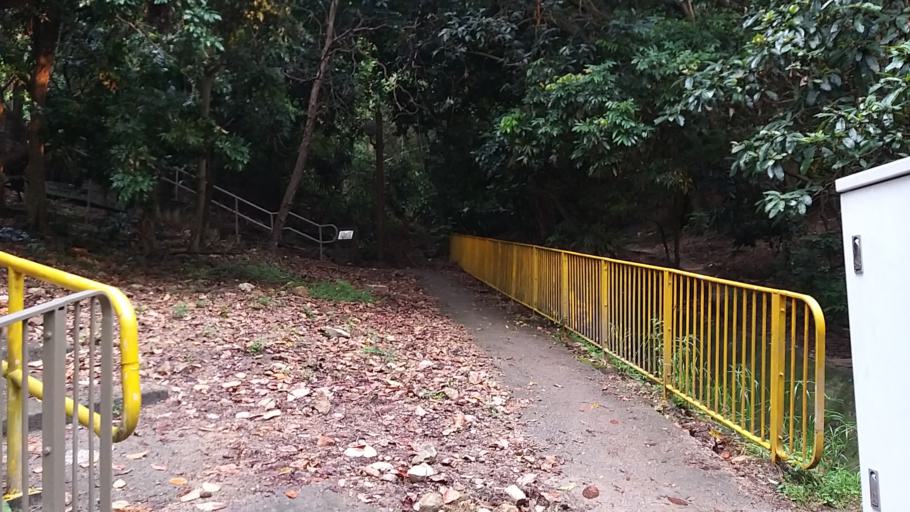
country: HK
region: Tuen Mun
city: Tuen Mun
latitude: 22.4040
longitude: 113.9820
